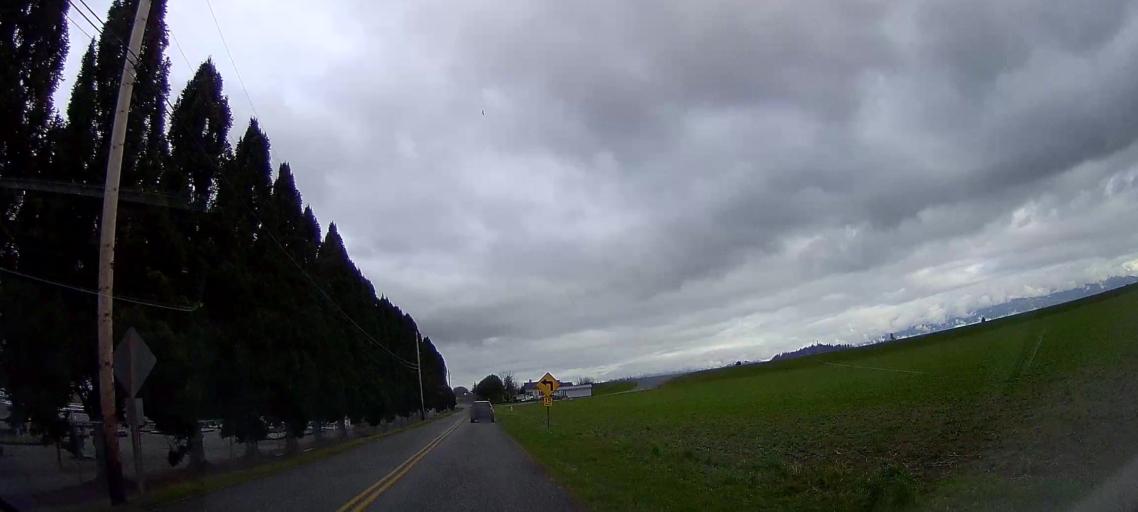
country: US
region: Washington
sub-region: Skagit County
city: Mount Vernon
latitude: 48.4443
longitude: -122.3575
